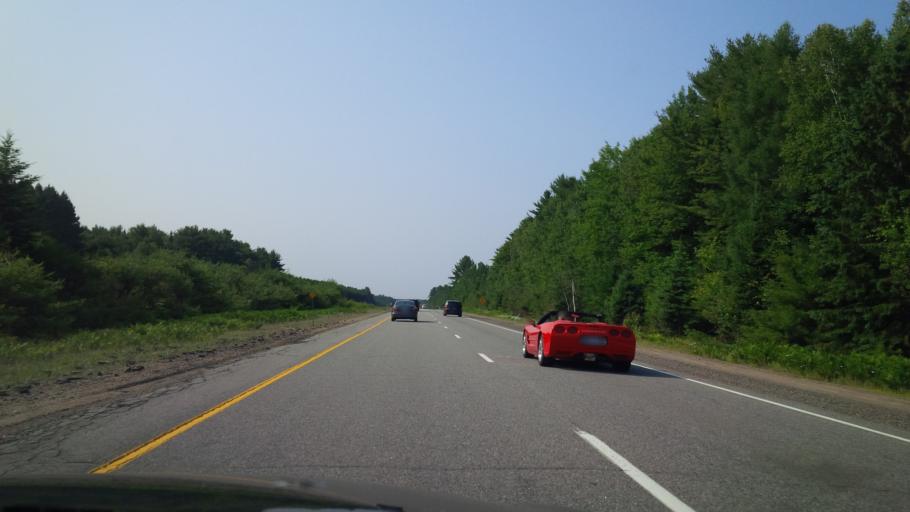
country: CA
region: Ontario
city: Bracebridge
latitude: 45.1306
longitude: -79.3112
